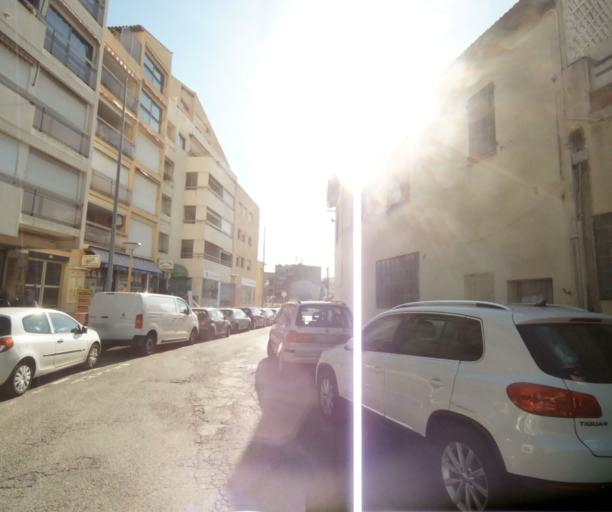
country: FR
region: Provence-Alpes-Cote d'Azur
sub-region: Departement des Alpes-Maritimes
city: Antibes
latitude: 43.5828
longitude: 7.1239
